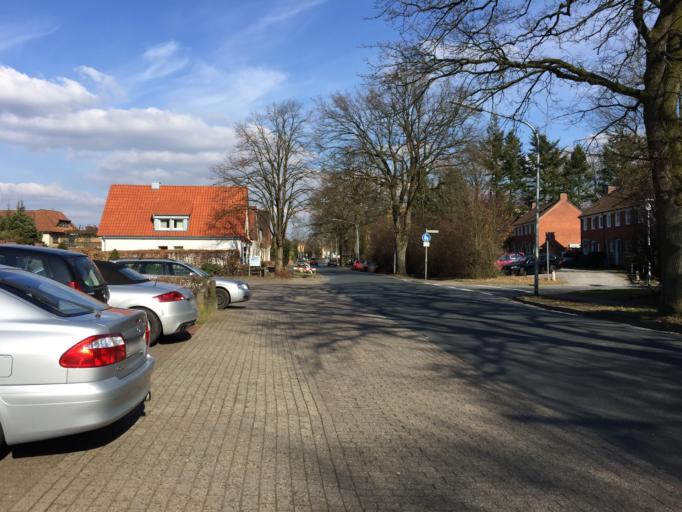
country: DE
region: Lower Saxony
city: Oldenburg
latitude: 53.1657
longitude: 8.2382
